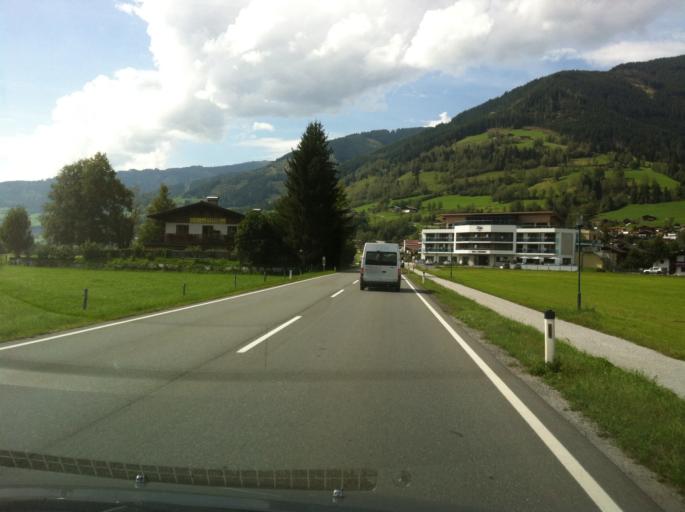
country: AT
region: Salzburg
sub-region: Politischer Bezirk Zell am See
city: Kaprun
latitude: 47.2865
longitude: 12.7489
